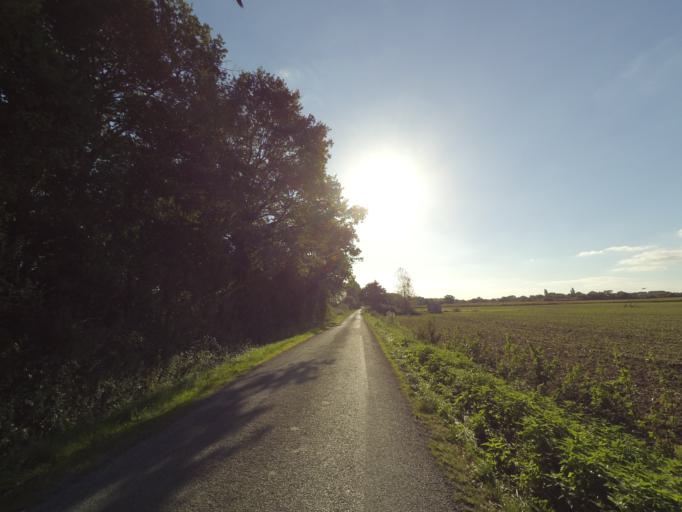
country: FR
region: Pays de la Loire
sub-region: Departement de la Loire-Atlantique
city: Chemere
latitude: 47.1366
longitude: -1.9153
